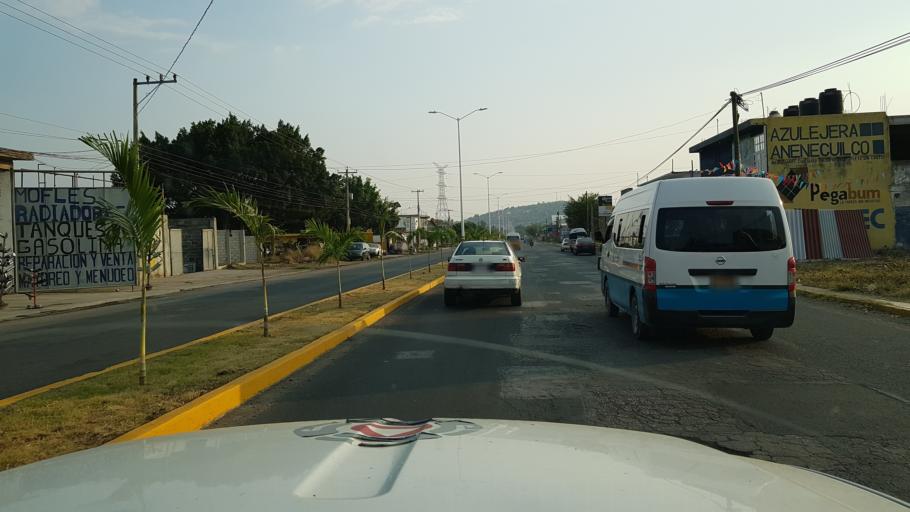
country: MX
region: Morelos
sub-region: Ayala
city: San Pedro Apatlaco
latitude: 18.7921
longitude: -98.9752
